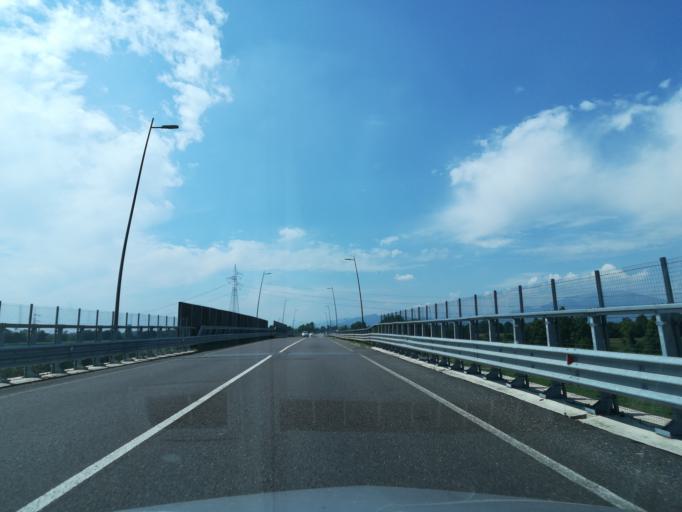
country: IT
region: Lombardy
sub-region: Provincia di Bergamo
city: Stezzano
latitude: 45.6371
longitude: 9.6459
